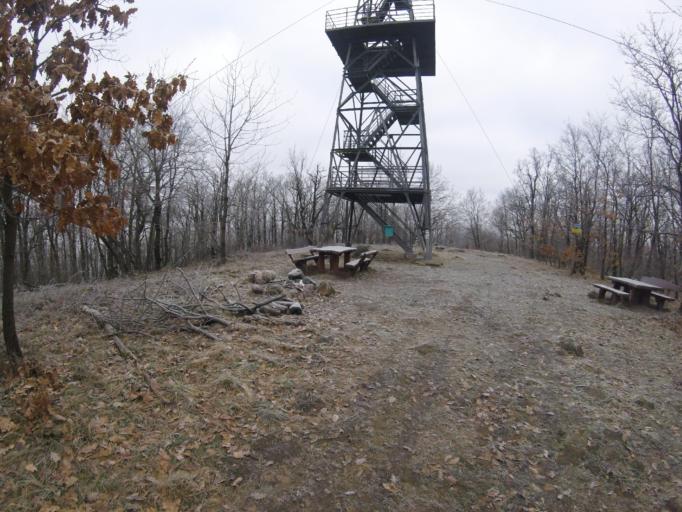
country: HU
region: Nograd
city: Paszto
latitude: 47.9489
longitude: 19.6368
